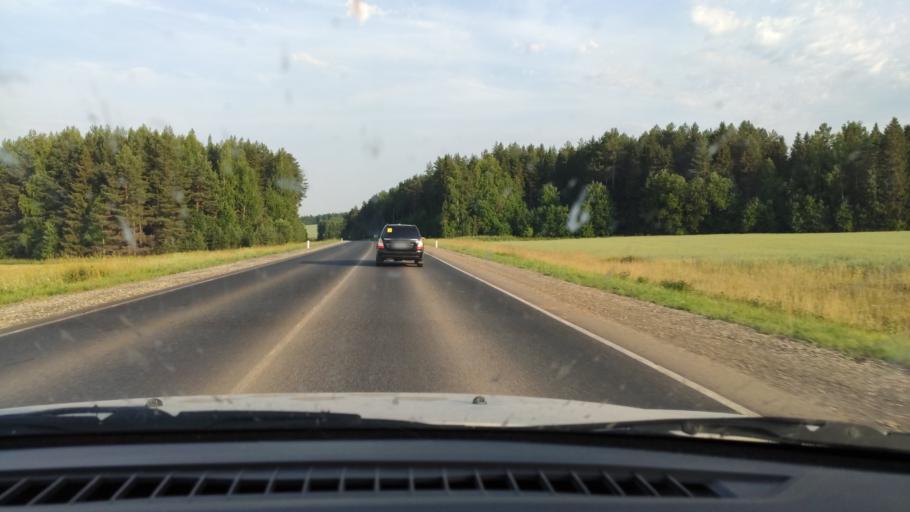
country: RU
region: Perm
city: Siva
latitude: 58.4096
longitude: 54.4720
